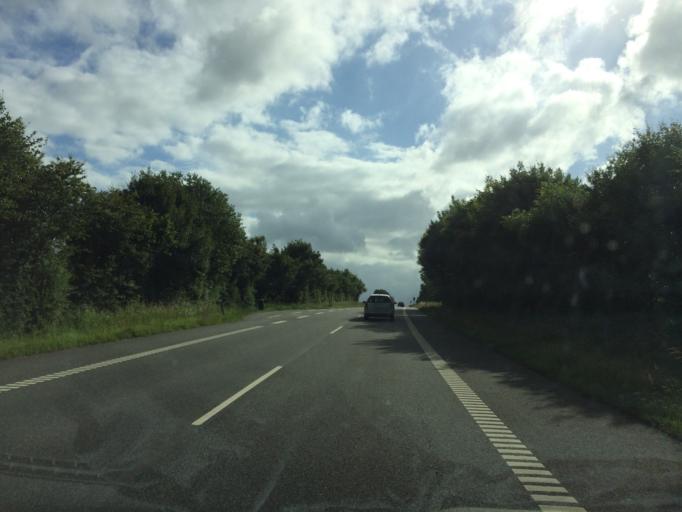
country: DK
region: South Denmark
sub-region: Sonderborg Kommune
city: Guderup
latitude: 54.9743
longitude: 9.9514
